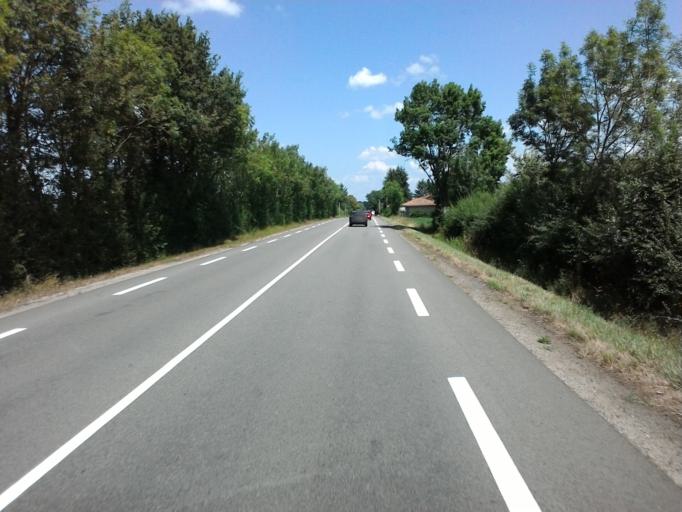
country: FR
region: Rhone-Alpes
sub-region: Departement de l'Ain
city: Saint-Etienne-du-Bois
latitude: 46.2754
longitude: 5.2858
